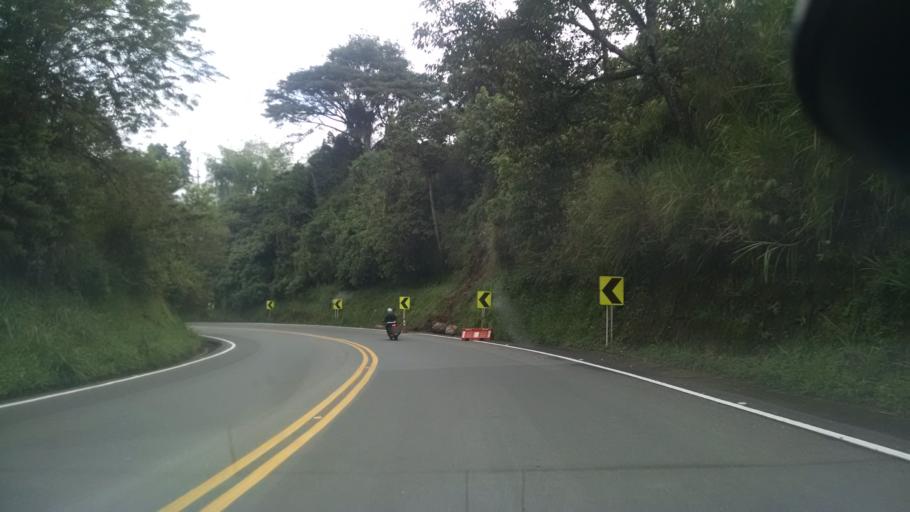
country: CO
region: Caldas
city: Palestina
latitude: 5.0187
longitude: -75.5933
